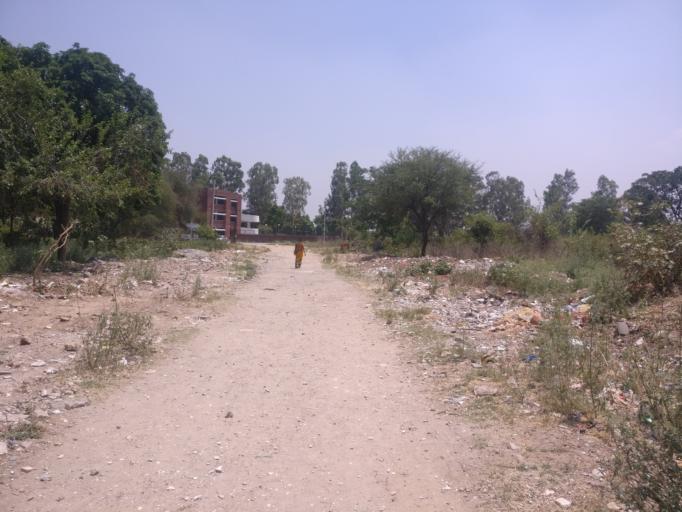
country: IN
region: Punjab
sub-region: Ajitgarh
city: Mohali
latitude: 30.7288
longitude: 76.7286
